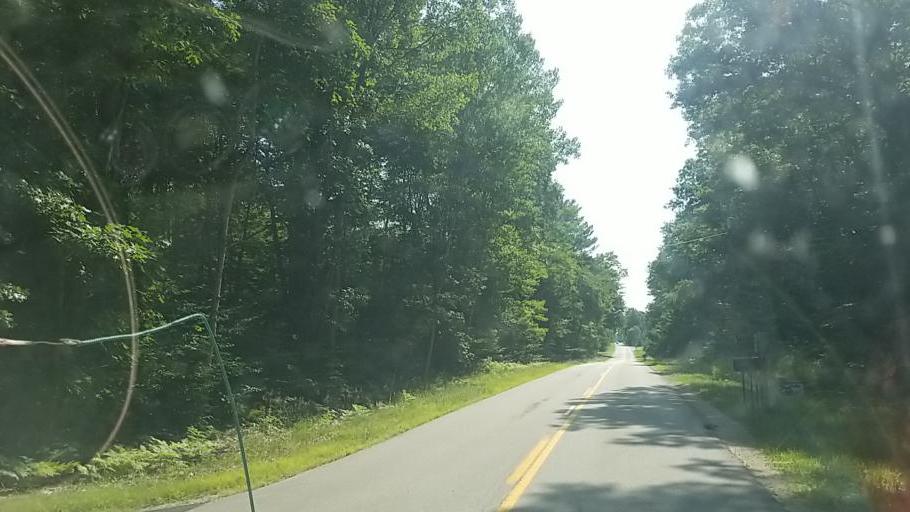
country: US
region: Michigan
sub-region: Muskegon County
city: Whitehall
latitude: 43.3705
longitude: -86.3602
